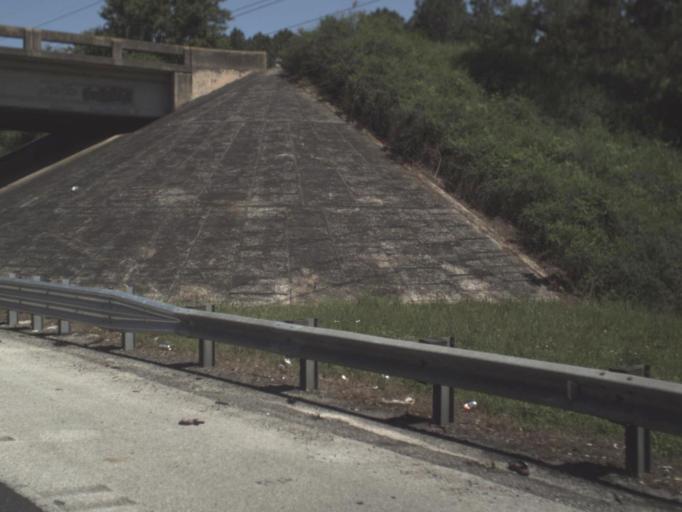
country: US
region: Florida
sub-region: Duval County
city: Baldwin
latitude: 30.2900
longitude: -81.9665
